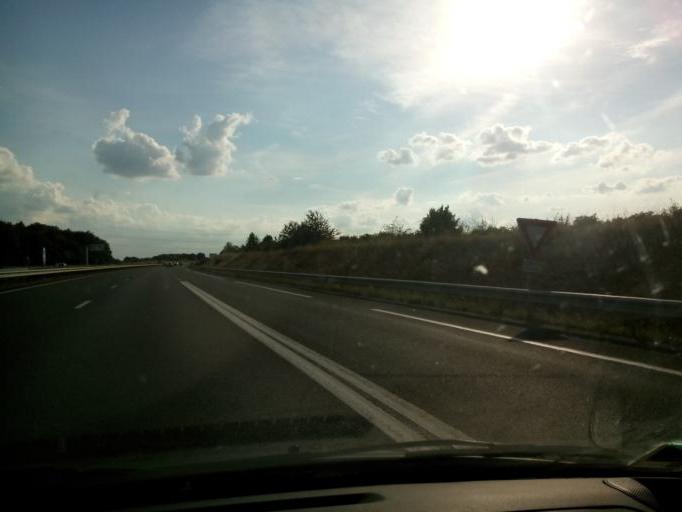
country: FR
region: Centre
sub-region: Departement d'Indre-et-Loire
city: Ballan-Mire
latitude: 47.3194
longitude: 0.5967
